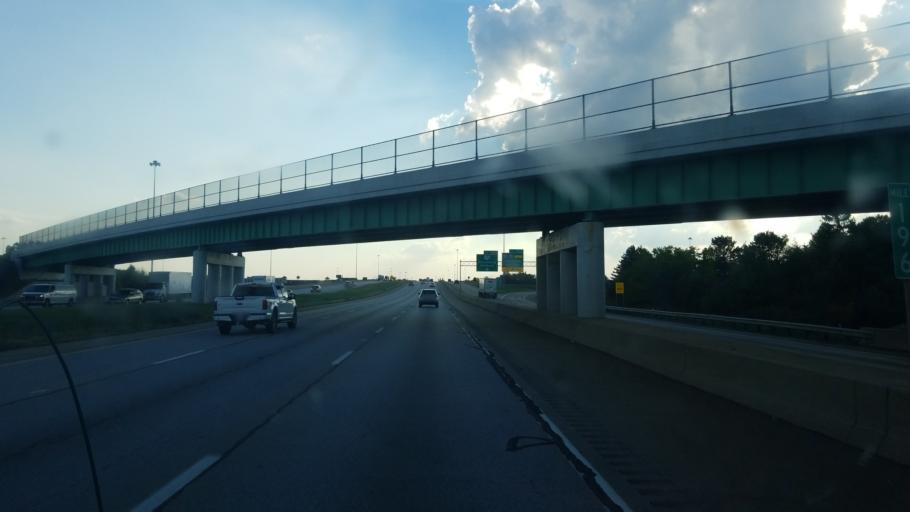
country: US
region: Ohio
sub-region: Wood County
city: Rossford
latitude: 41.5737
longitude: -83.5768
